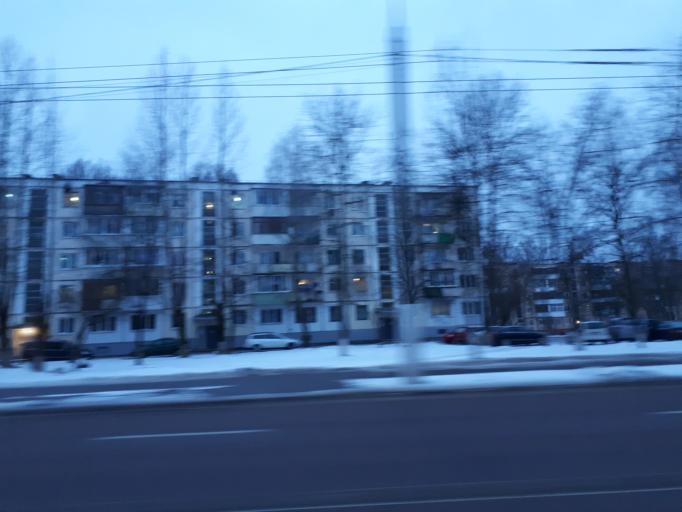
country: BY
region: Vitebsk
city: Vitebsk
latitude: 55.1865
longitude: 30.2207
